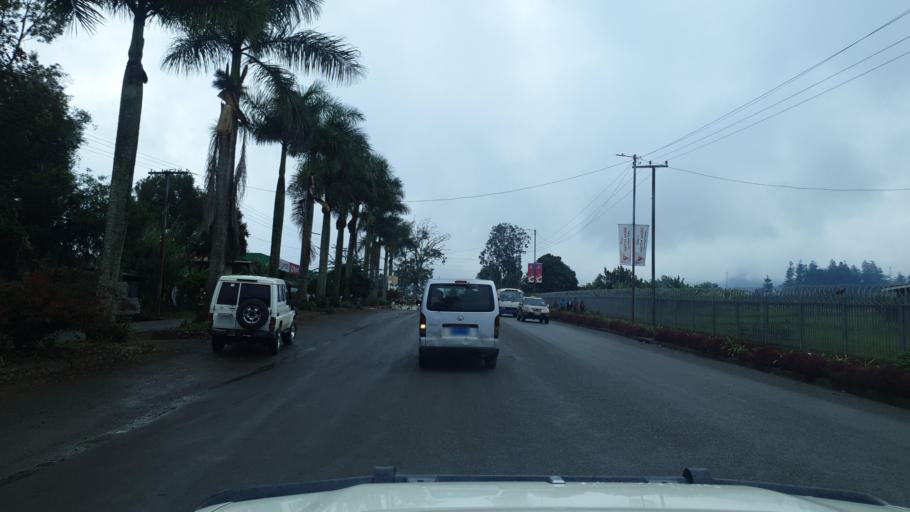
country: PG
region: Eastern Highlands
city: Goroka
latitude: -6.0785
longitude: 145.3894
